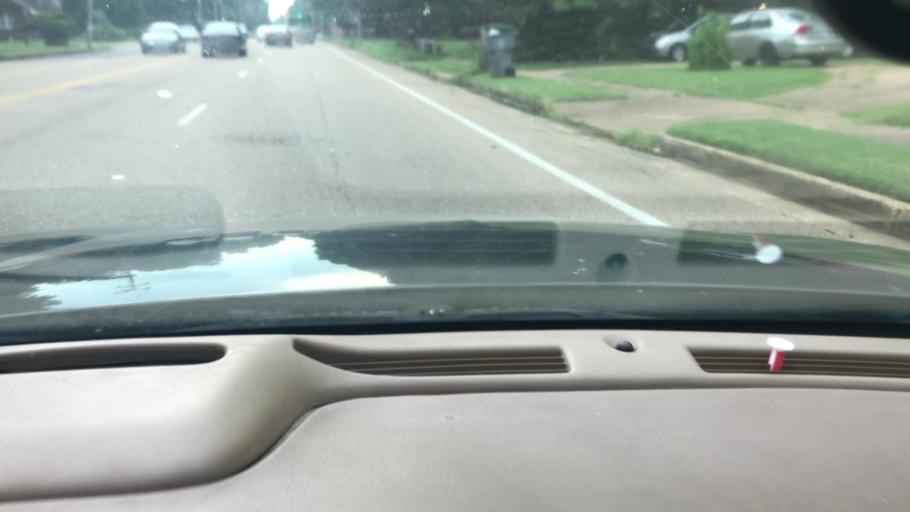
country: US
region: Tennessee
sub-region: Shelby County
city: Germantown
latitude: 35.0622
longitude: -89.8957
